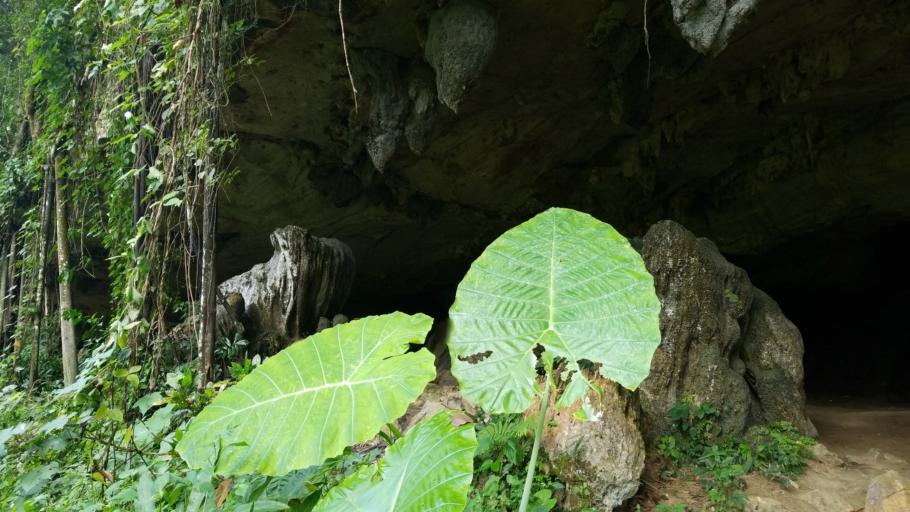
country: TH
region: Yala
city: Betong
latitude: 5.6643
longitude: 100.8864
